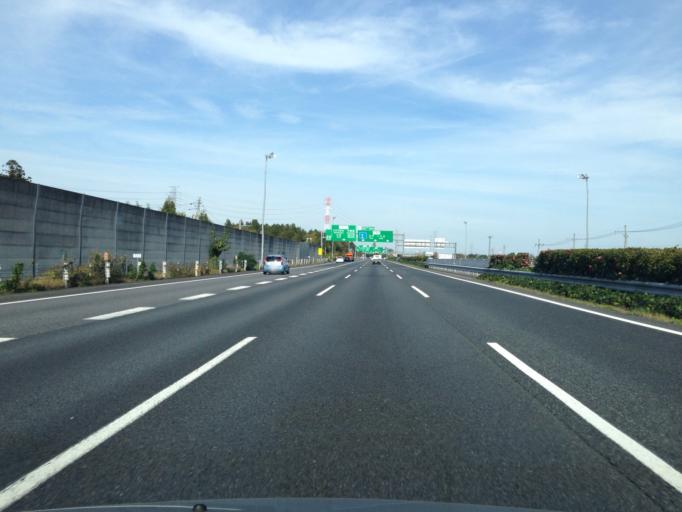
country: JP
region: Ibaraki
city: Tomobe
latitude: 36.3140
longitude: 140.3428
